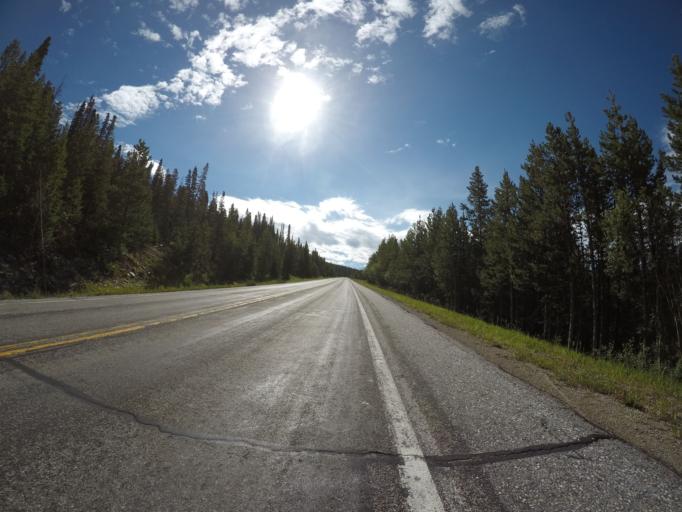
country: US
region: Wyoming
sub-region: Carbon County
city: Saratoga
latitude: 41.3266
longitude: -106.4707
